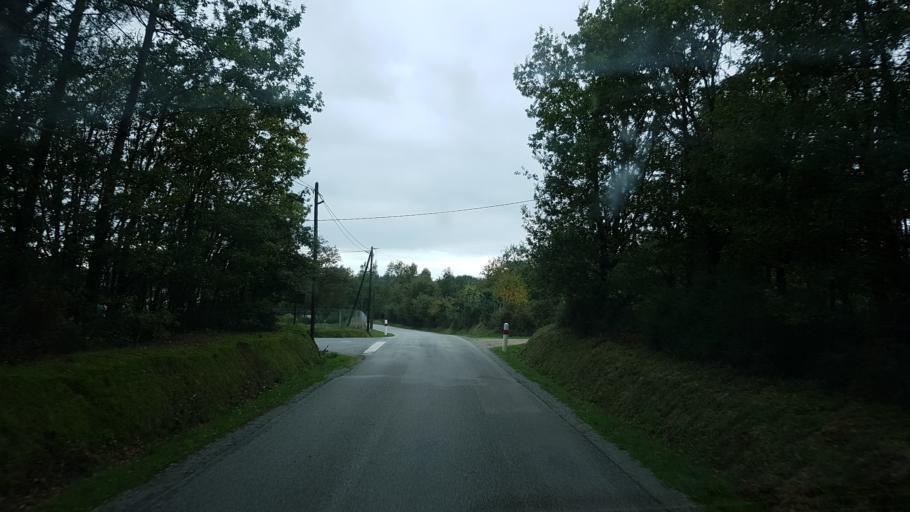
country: FR
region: Brittany
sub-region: Departement du Morbihan
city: Serent
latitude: 47.7814
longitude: -2.4888
